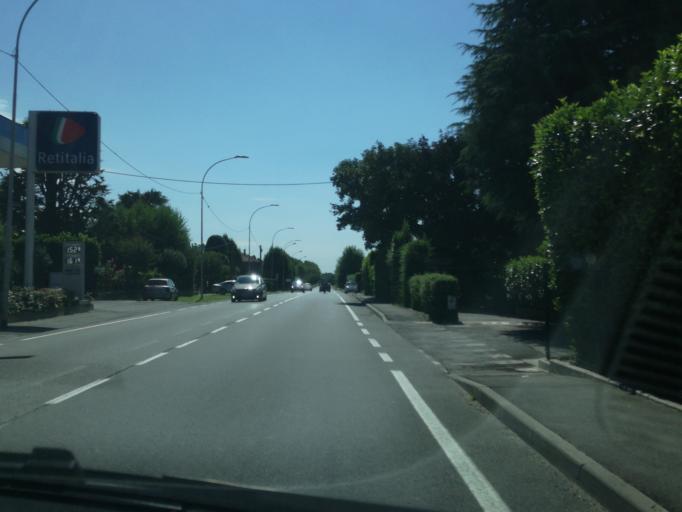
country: IT
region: Lombardy
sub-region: Provincia di Bergamo
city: Piazza Caduti
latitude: 45.6988
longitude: 9.4972
